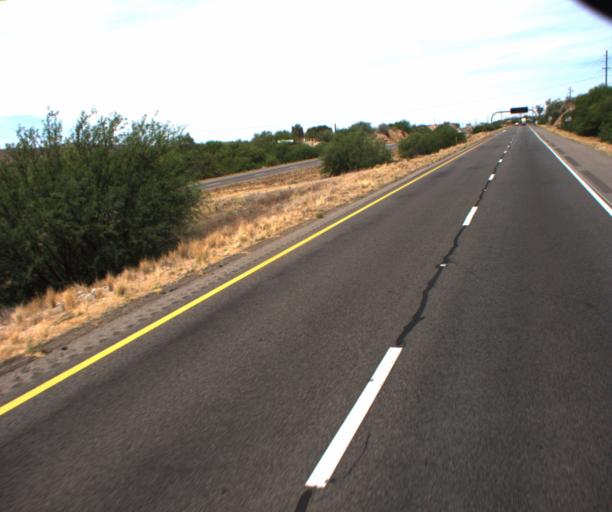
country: US
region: Arizona
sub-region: Maricopa County
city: Wickenburg
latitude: 33.9346
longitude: -112.6916
